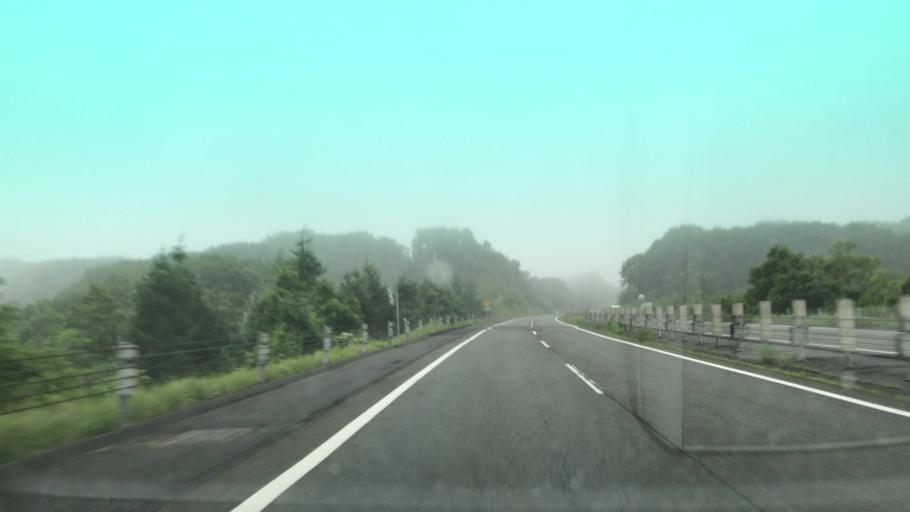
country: JP
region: Hokkaido
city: Tomakomai
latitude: 42.6551
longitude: 141.5704
